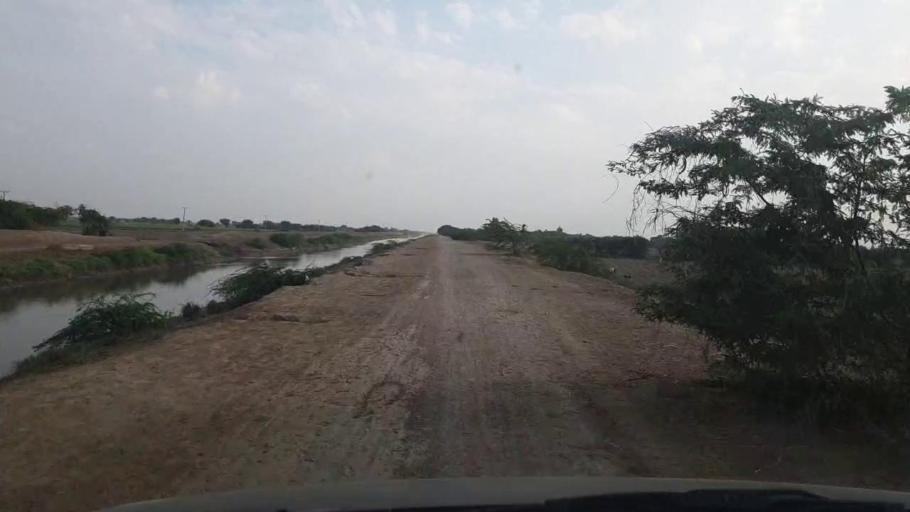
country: PK
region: Sindh
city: Badin
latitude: 24.5281
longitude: 68.6794
